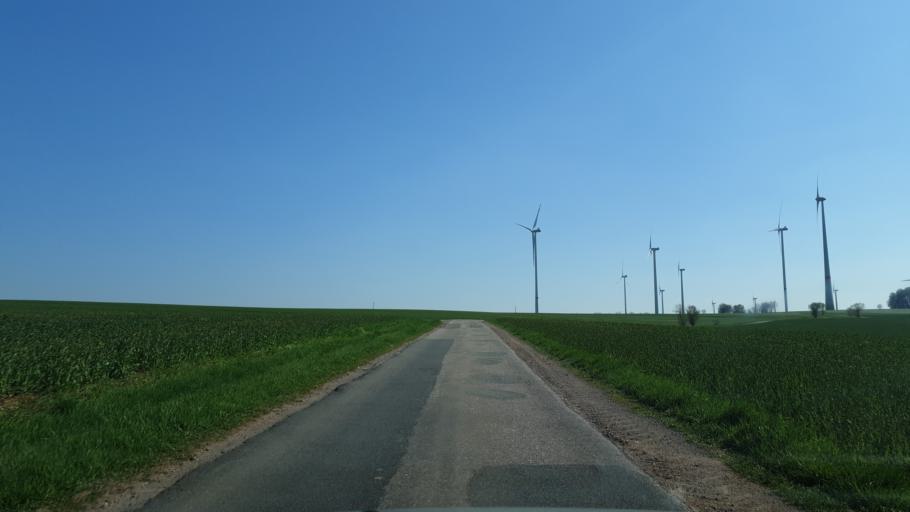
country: DE
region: Saxony
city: Bernsdorf
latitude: 50.7750
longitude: 12.6844
